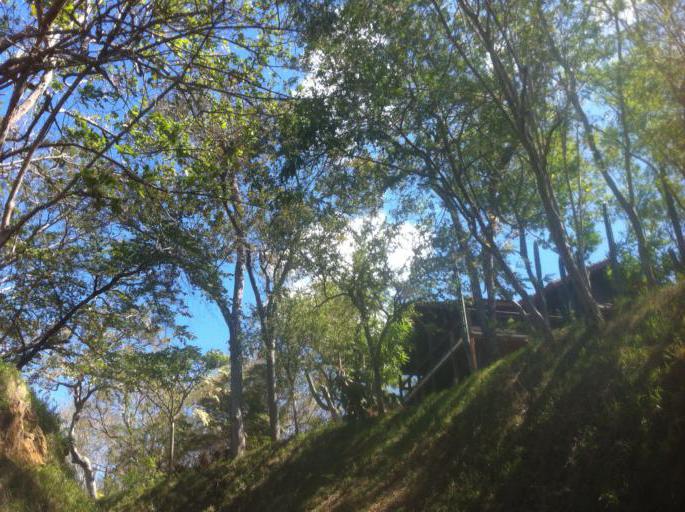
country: NI
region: Rivas
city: Tola
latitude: 11.3797
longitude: -86.0316
